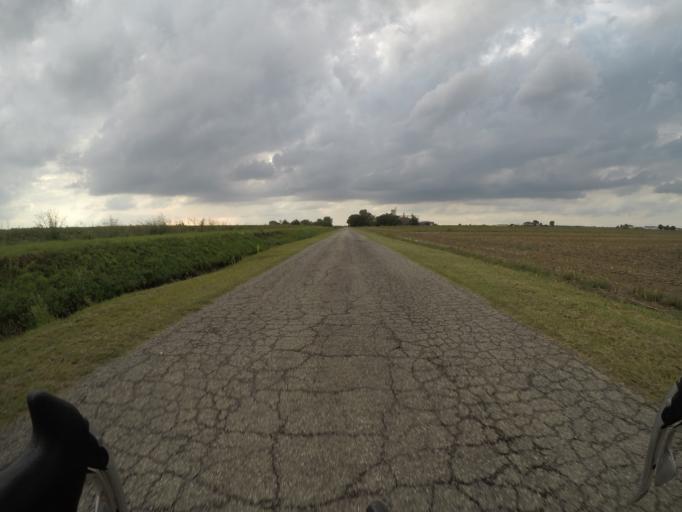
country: IT
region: Veneto
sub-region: Provincia di Rovigo
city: Polesella
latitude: 44.9663
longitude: 11.7281
